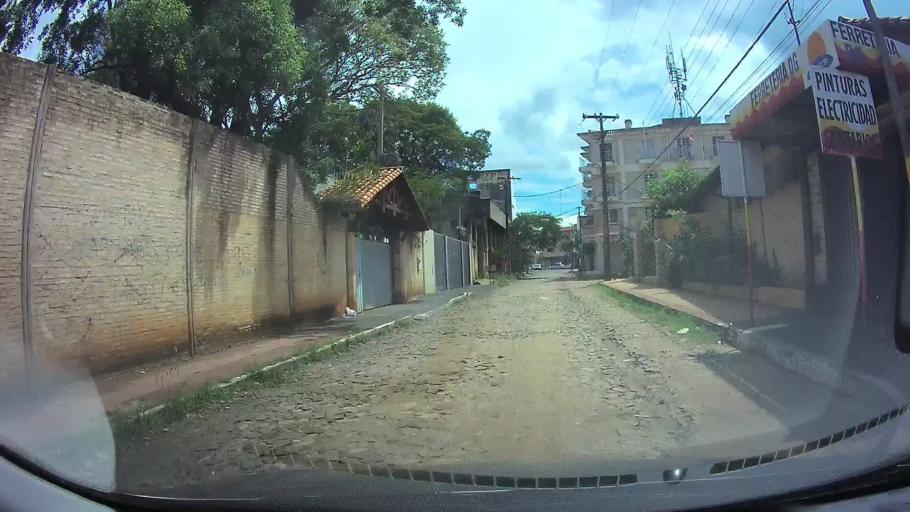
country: PY
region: Central
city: Fernando de la Mora
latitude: -25.3159
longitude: -57.5255
